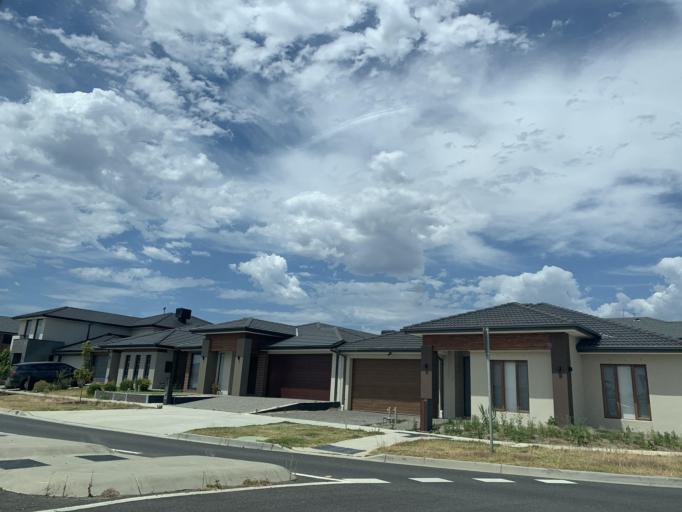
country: AU
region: Victoria
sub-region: Casey
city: Cranbourne South
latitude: -38.1254
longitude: 145.2360
